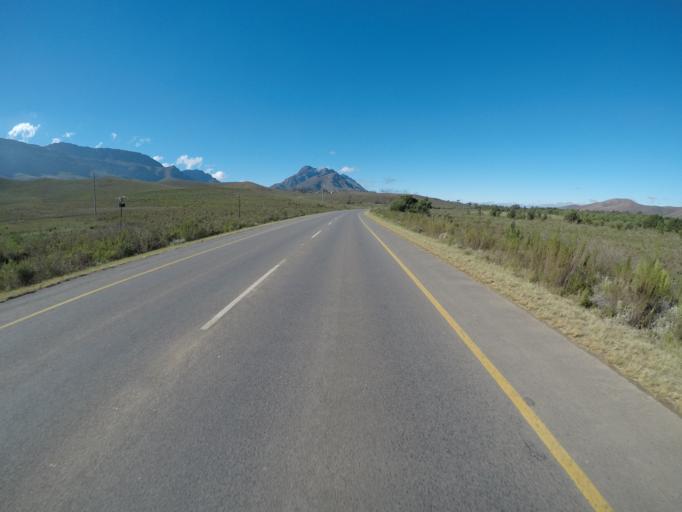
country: ZA
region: Western Cape
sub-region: Overberg District Municipality
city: Caledon
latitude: -34.0490
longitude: 19.5802
